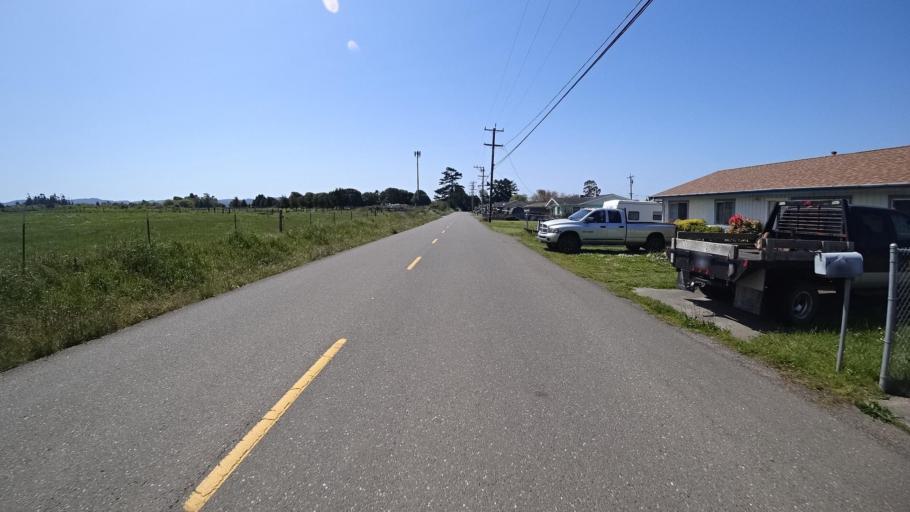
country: US
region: California
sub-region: Humboldt County
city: Fortuna
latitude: 40.5630
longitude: -124.1364
